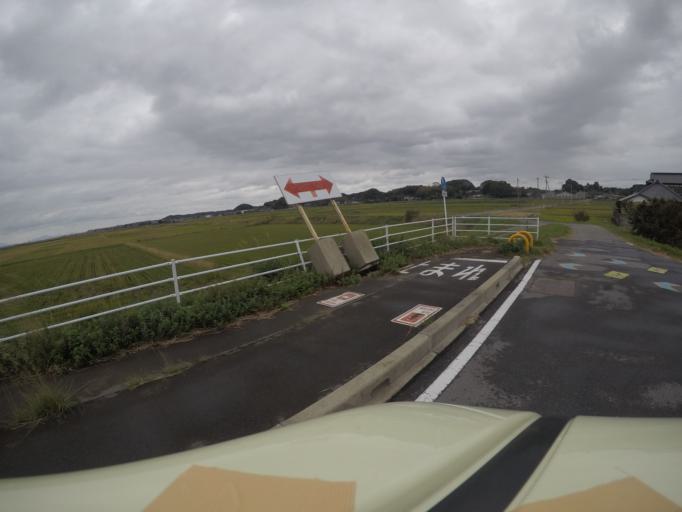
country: JP
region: Ibaraki
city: Itako
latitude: 36.0133
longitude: 140.4649
